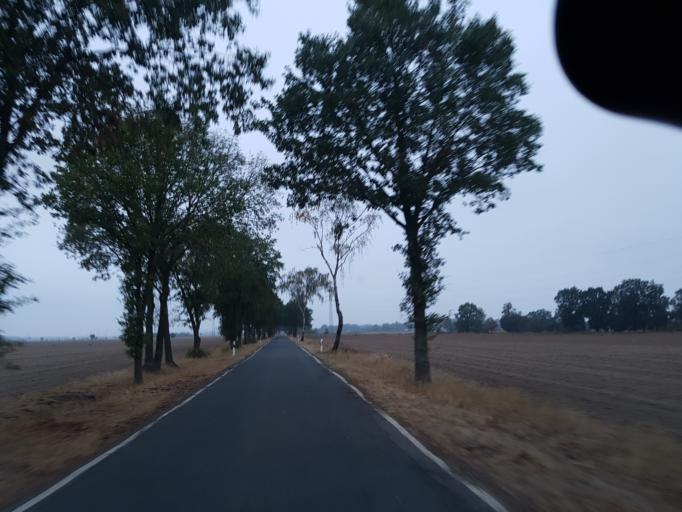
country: DE
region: Saxony-Anhalt
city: Annaburg
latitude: 51.7705
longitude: 13.0680
